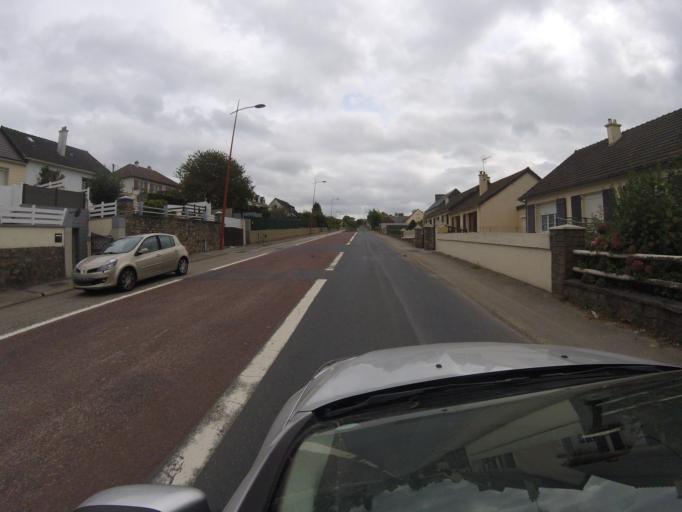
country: FR
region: Lower Normandy
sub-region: Departement de la Manche
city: La Glacerie
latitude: 49.6156
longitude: -1.6058
